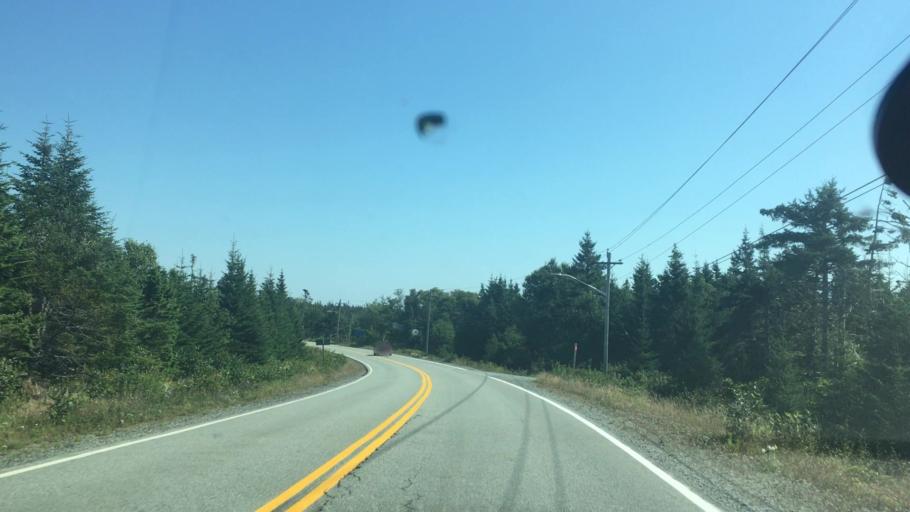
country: CA
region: Nova Scotia
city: Antigonish
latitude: 44.9342
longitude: -62.2748
